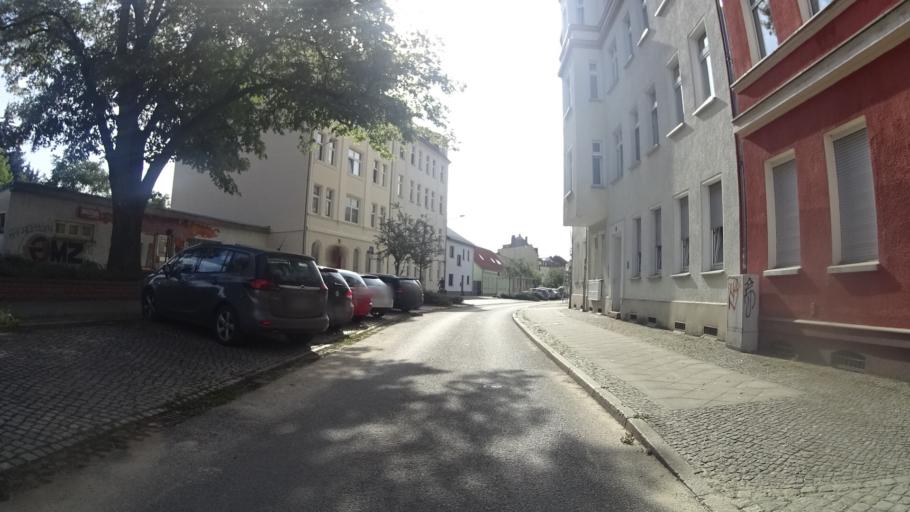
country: DE
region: Brandenburg
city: Brandenburg an der Havel
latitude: 52.4139
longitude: 12.5394
